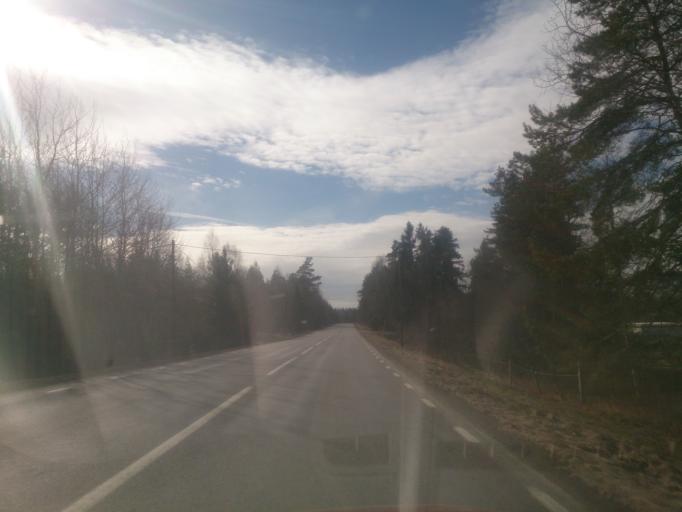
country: SE
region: OEstergoetland
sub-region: Finspangs Kommun
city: Finspang
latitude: 58.6274
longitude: 15.8216
